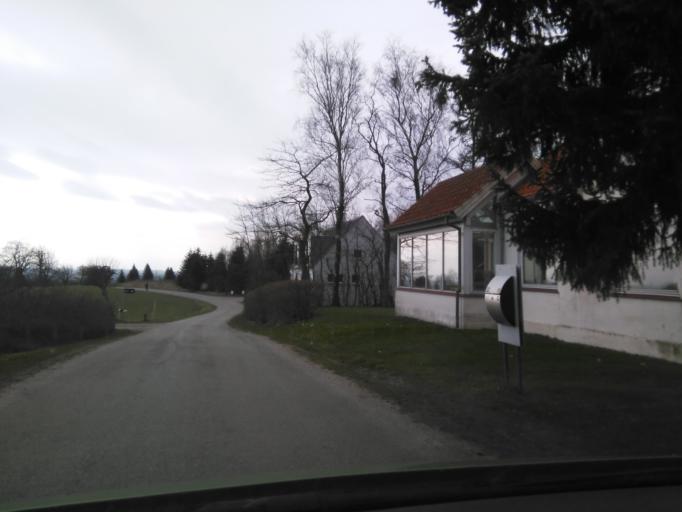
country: DK
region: Central Jutland
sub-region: Arhus Kommune
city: Malling
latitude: 56.0341
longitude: 10.2155
